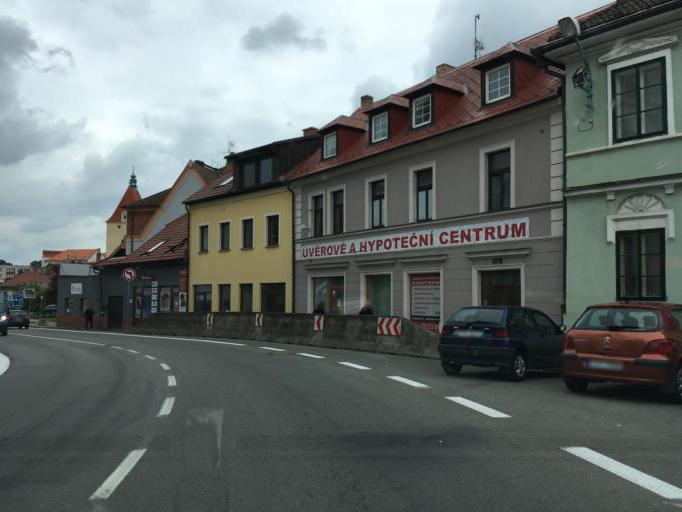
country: CZ
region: Vysocina
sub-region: Okres Pelhrimov
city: Pelhrimov
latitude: 49.4328
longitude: 15.2230
